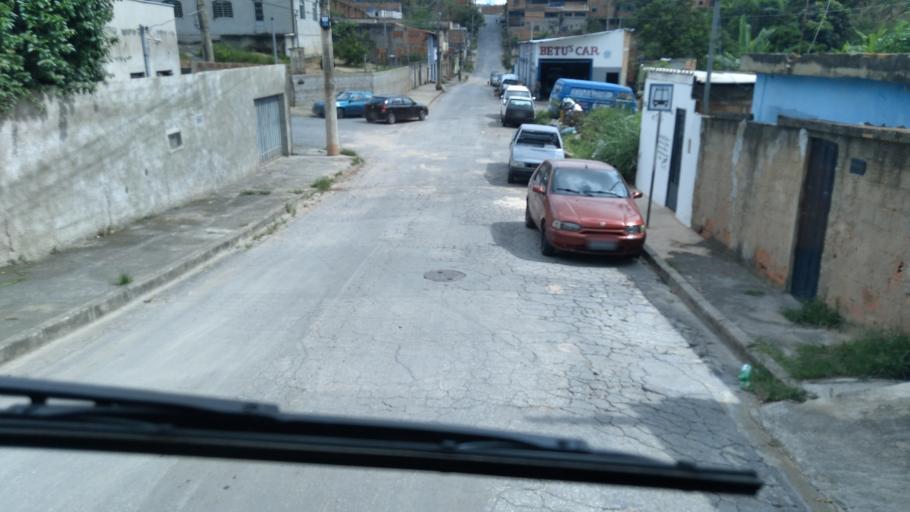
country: BR
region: Minas Gerais
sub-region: Santa Luzia
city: Santa Luzia
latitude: -19.8322
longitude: -43.8948
